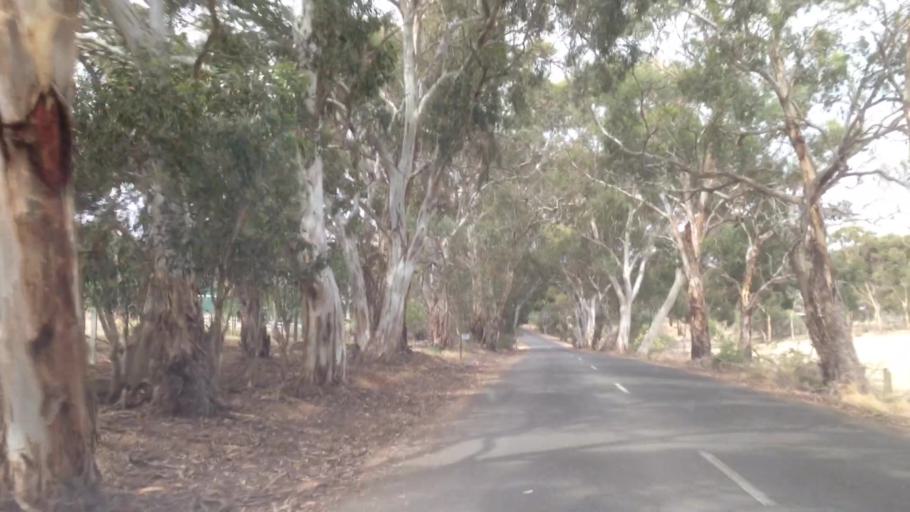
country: AU
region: South Australia
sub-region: Barossa
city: Williamstown
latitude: -34.6430
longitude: 138.8522
